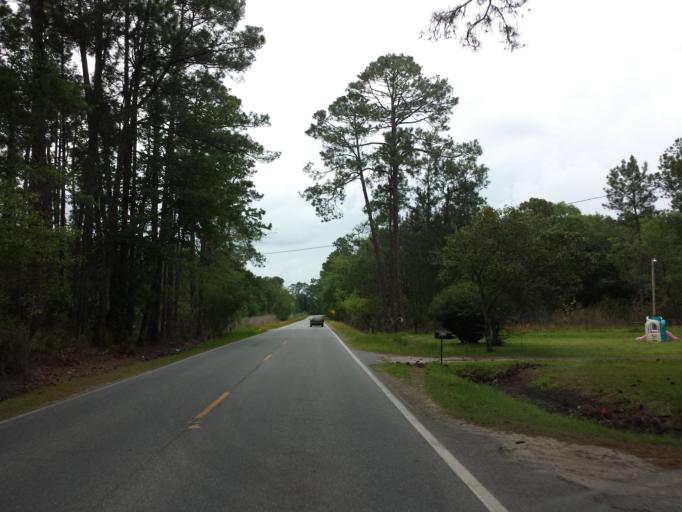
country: US
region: Georgia
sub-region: Cook County
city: Sparks
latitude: 31.2416
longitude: -83.4627
